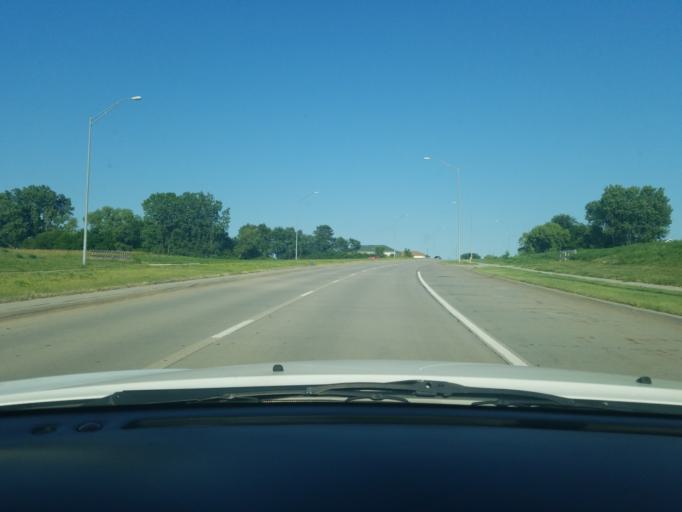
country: US
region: Nebraska
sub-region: Lancaster County
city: Lincoln
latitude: 40.7414
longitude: -96.6039
